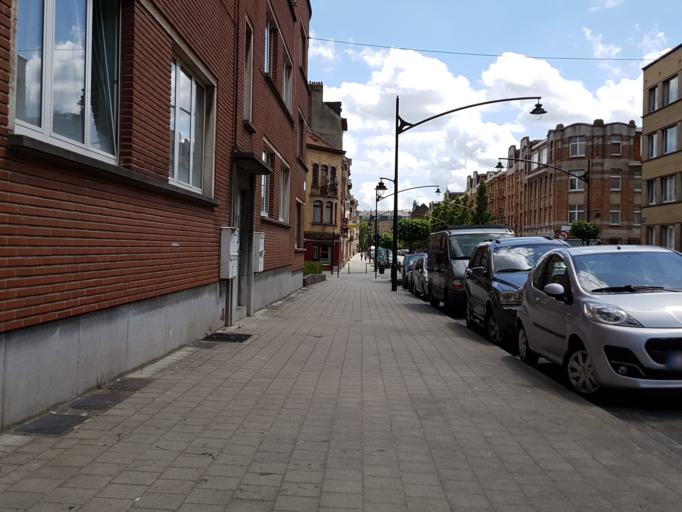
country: BE
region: Brussels Capital
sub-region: Bruxelles-Capitale
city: Brussels
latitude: 50.8833
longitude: 4.3429
